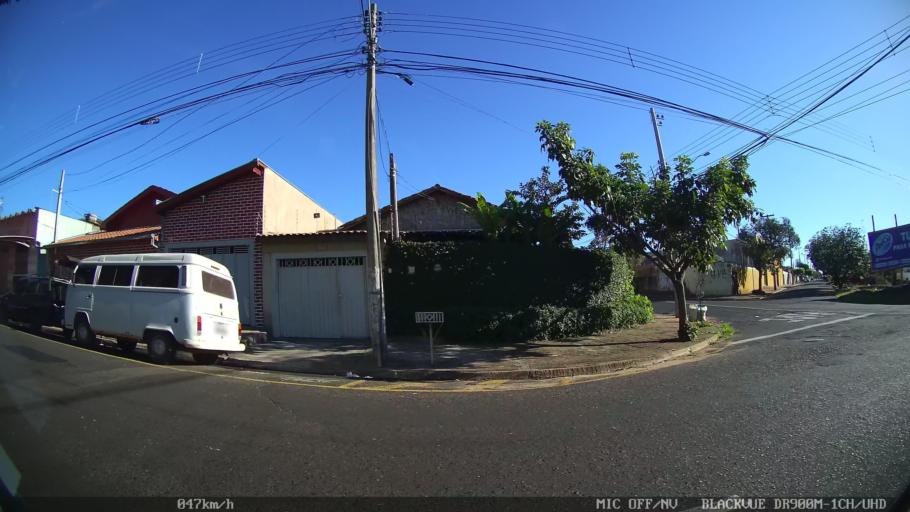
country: BR
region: Sao Paulo
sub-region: Franca
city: Franca
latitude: -20.5793
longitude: -47.3774
